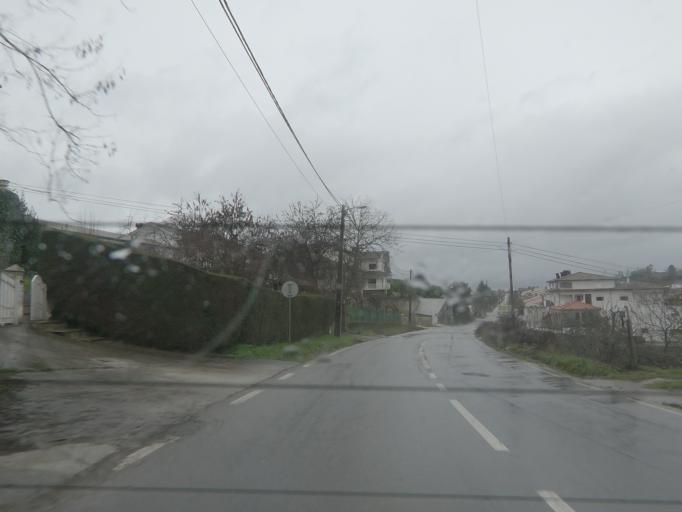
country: PT
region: Vila Real
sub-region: Vila Real
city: Vila Real
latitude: 41.2683
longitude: -7.7025
